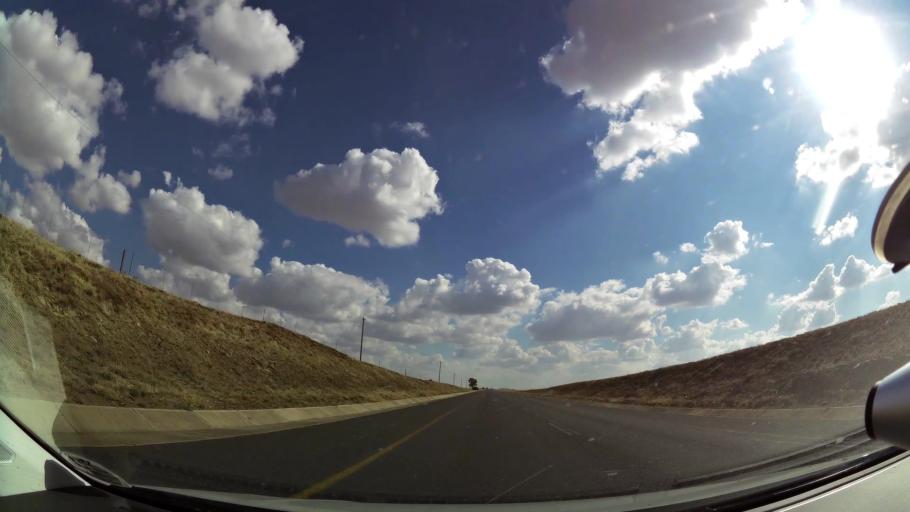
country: ZA
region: Orange Free State
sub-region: Mangaung Metropolitan Municipality
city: Bloemfontein
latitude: -29.1563
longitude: 25.7391
